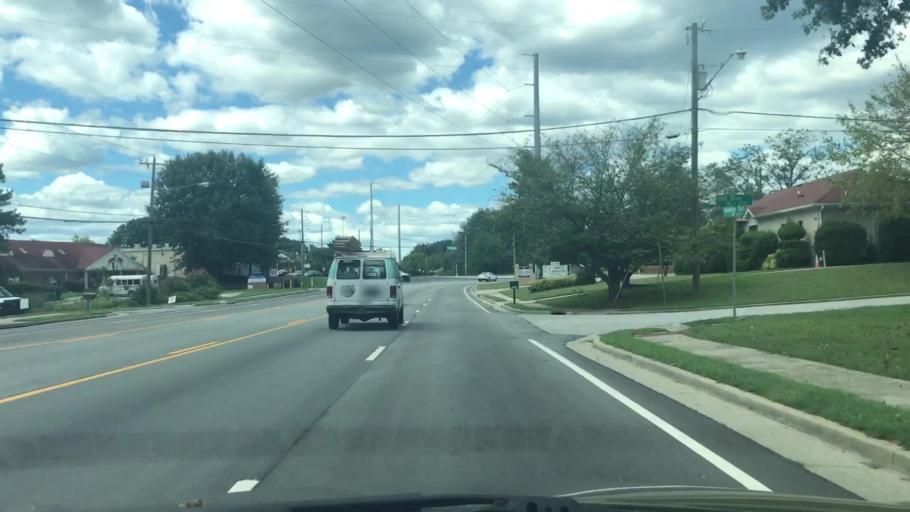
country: US
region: Georgia
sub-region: Gwinnett County
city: Mountain Park
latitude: 33.8201
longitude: -84.1107
